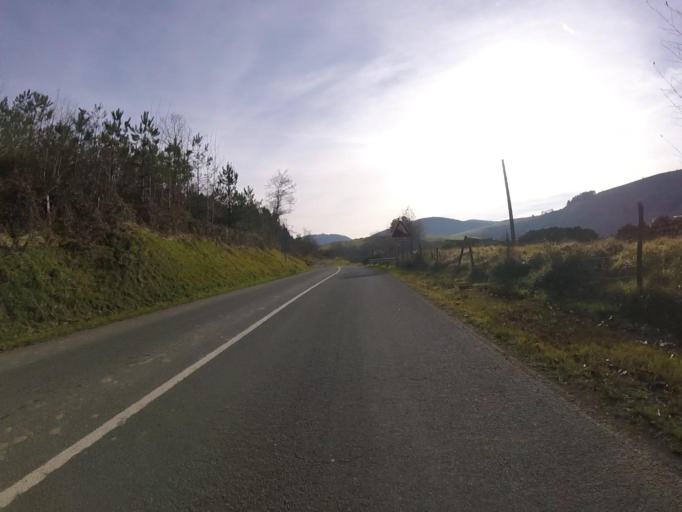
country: ES
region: Navarre
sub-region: Provincia de Navarra
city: Areso
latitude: 43.1023
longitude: -1.9538
